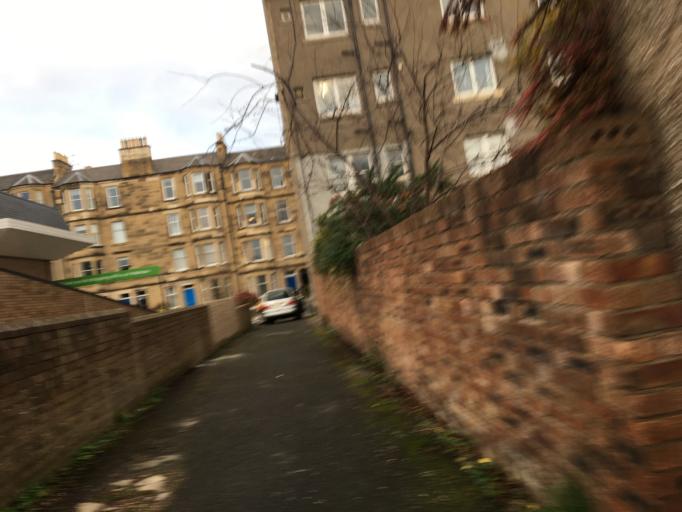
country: GB
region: Scotland
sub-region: Edinburgh
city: Edinburgh
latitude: 55.9297
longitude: -3.2082
